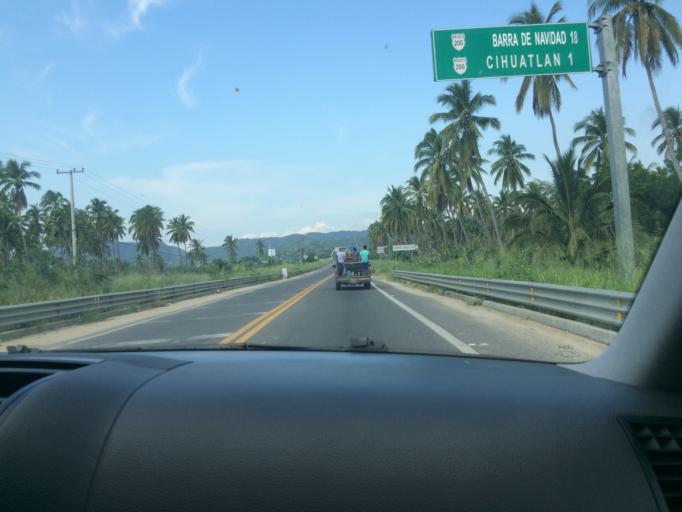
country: MX
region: Jalisco
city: Cihuatlan
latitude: 19.2335
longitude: -104.5492
